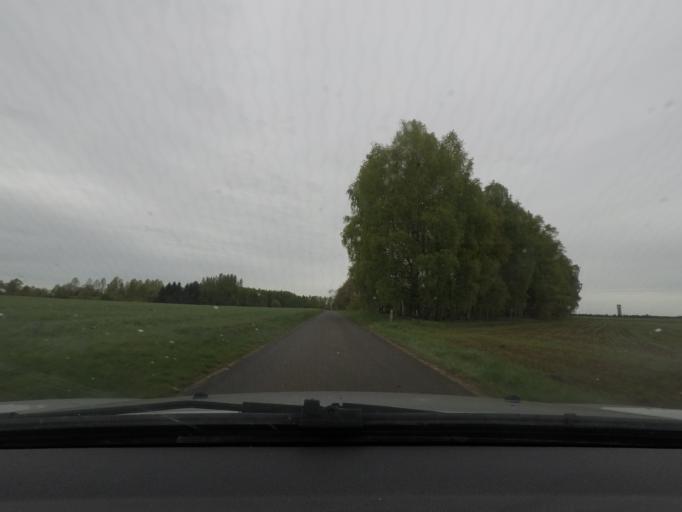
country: BE
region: Wallonia
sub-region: Province du Luxembourg
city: Etalle
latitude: 49.6572
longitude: 5.5559
